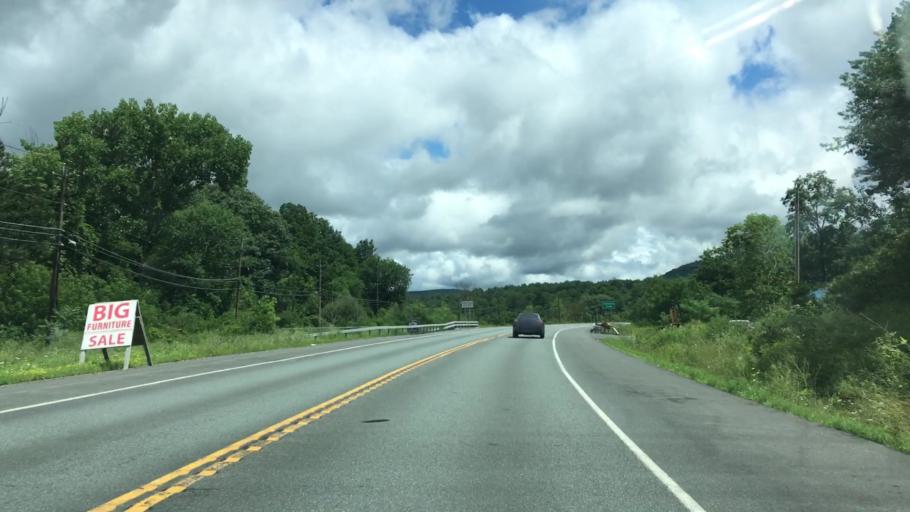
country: US
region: New York
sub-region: Rensselaer County
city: Hoosick Falls
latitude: 42.8463
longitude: -73.4669
